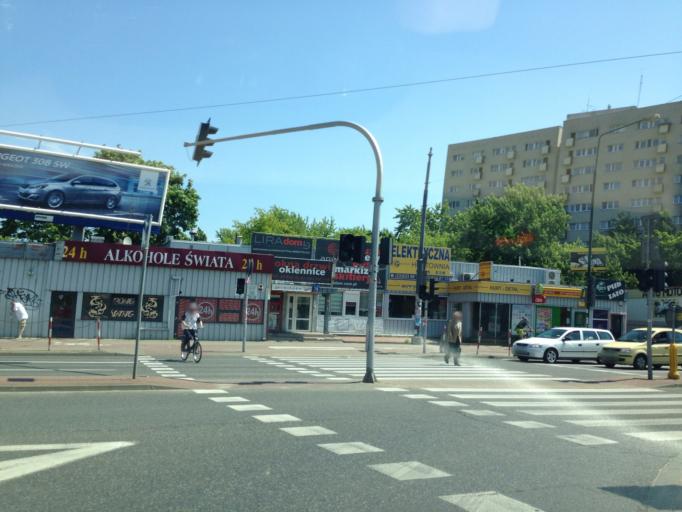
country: PL
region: Masovian Voivodeship
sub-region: Warszawa
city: Bielany
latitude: 52.2752
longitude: 20.9385
